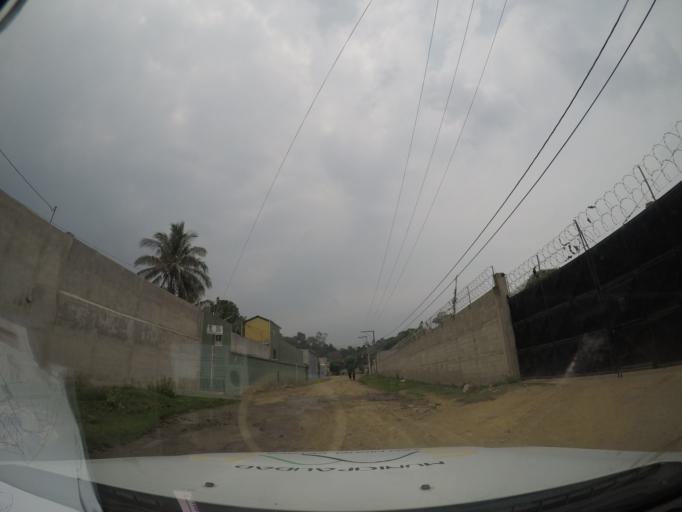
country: GT
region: Guatemala
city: Petapa
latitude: 14.5074
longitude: -90.5542
